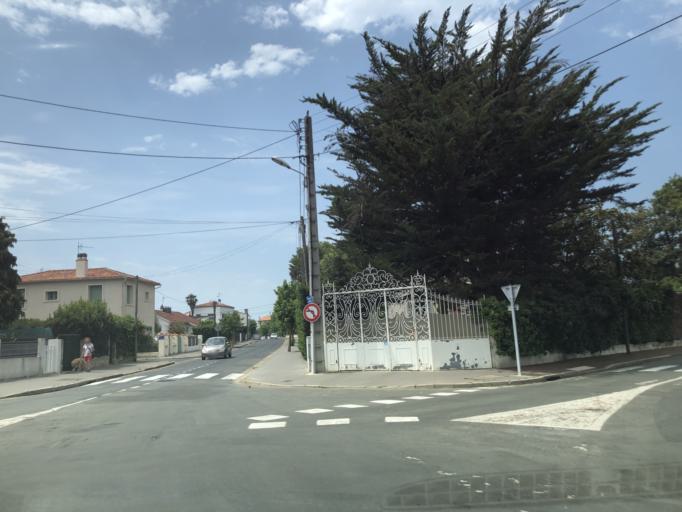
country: FR
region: Poitou-Charentes
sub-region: Departement de la Charente-Maritime
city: Royan
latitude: 45.6251
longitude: -1.0411
